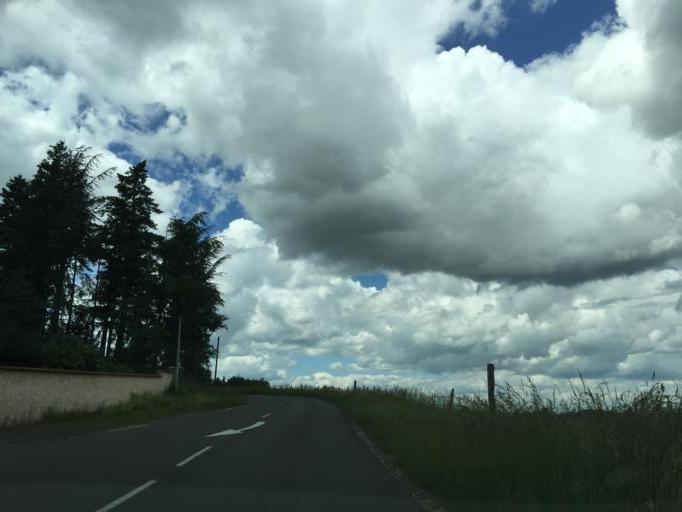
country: FR
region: Rhone-Alpes
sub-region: Departement de la Loire
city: Saint-Georges-Haute-Ville
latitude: 45.5141
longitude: 4.1011
